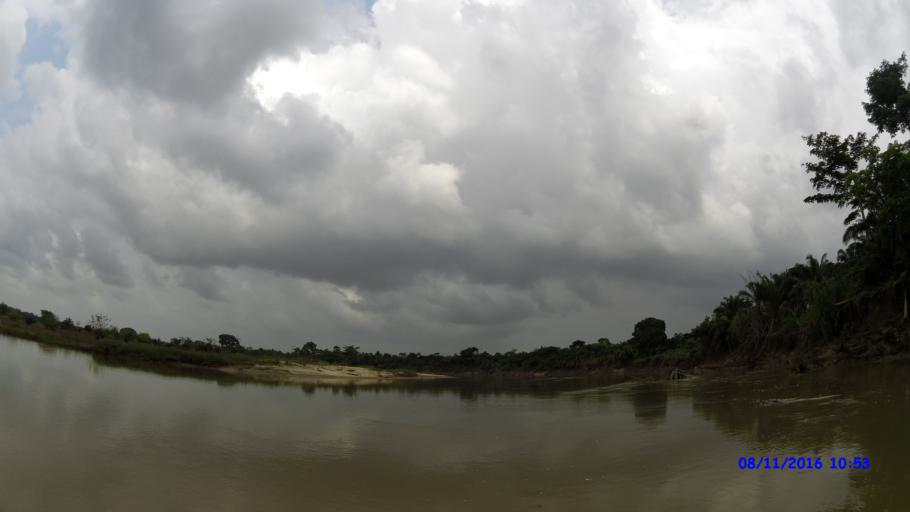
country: BJ
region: Mono
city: Lokossa
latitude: 6.4884
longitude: 1.7255
